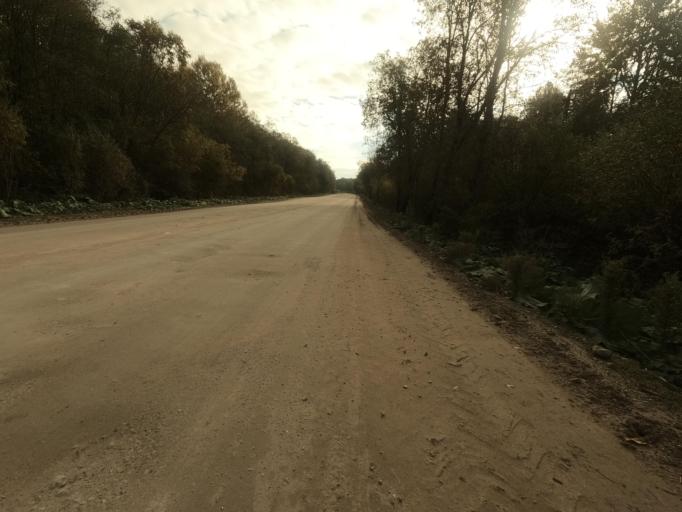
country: RU
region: Novgorod
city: Batetskiy
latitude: 58.7997
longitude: 30.6323
